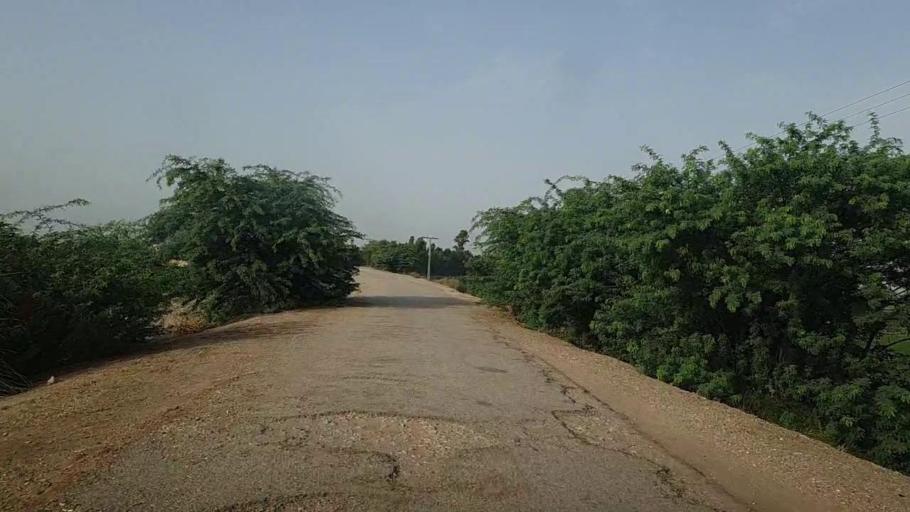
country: PK
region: Sindh
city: Mehar
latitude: 27.1290
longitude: 67.7894
